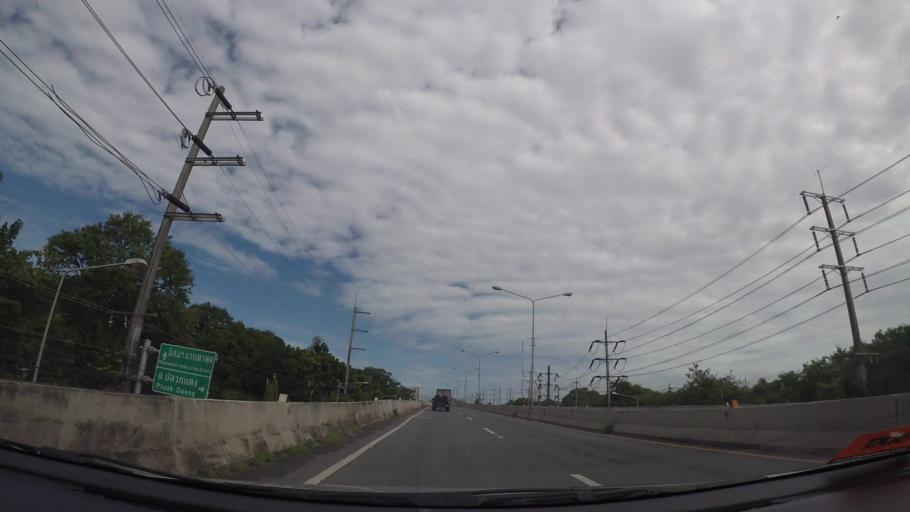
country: TH
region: Rayong
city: Ban Chang
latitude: 12.7261
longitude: 101.1466
